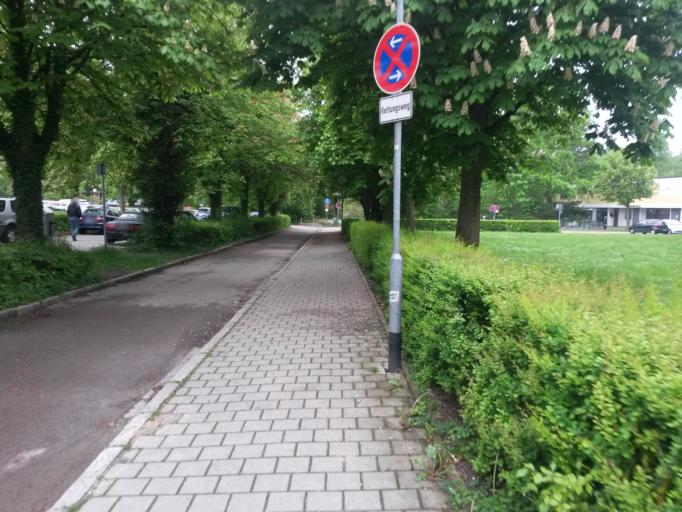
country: DE
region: Bavaria
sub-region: Upper Bavaria
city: Ingolstadt
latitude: 48.7620
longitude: 11.4190
